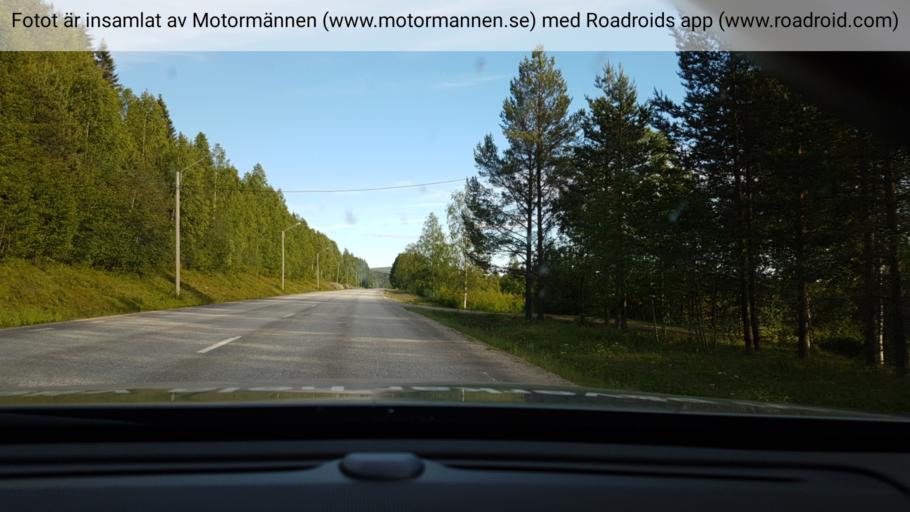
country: SE
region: Vaesterbotten
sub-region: Vannas Kommun
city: Vannasby
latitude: 64.1346
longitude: 19.9487
